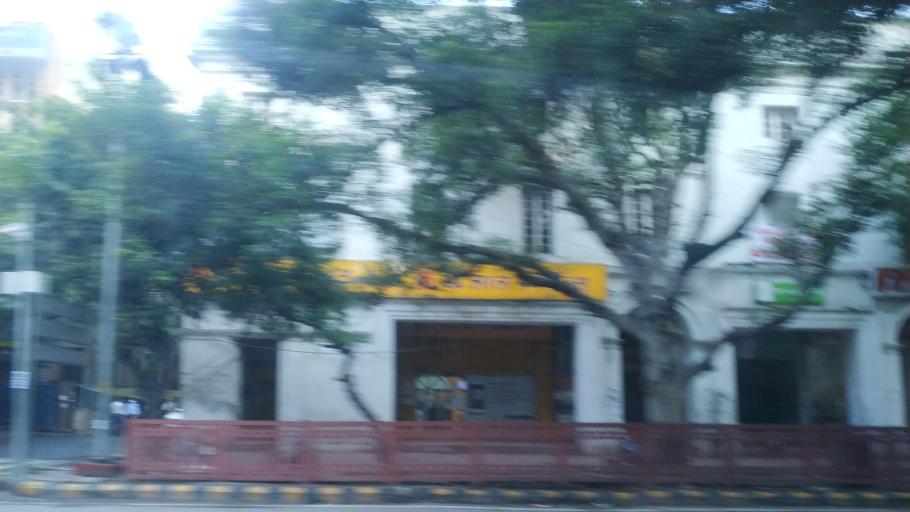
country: IN
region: NCT
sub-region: New Delhi
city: New Delhi
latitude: 28.6295
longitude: 77.2173
